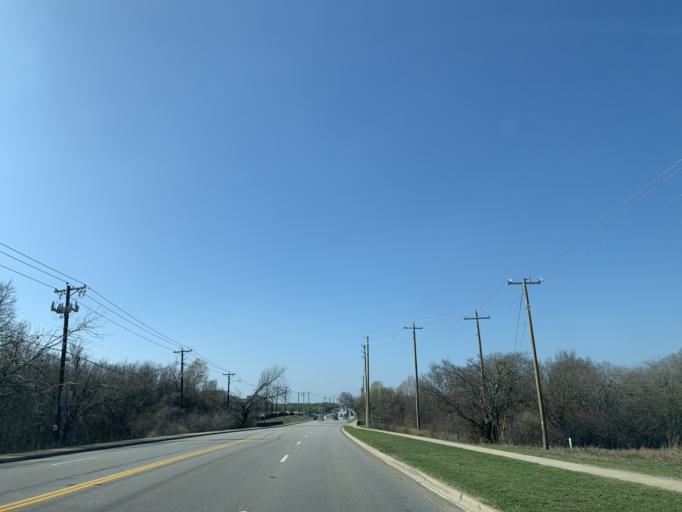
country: US
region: Texas
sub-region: Travis County
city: Windemere
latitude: 30.4965
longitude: -97.6323
